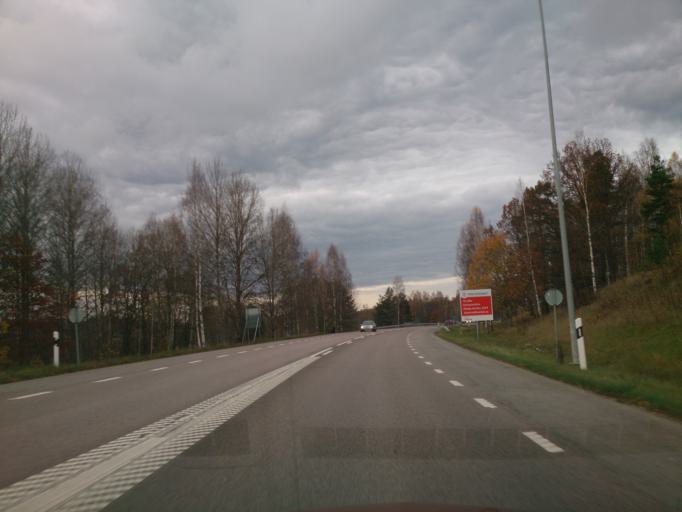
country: SE
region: OEstergoetland
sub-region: Atvidabergs Kommun
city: Atvidaberg
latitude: 58.2155
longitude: 15.9768
